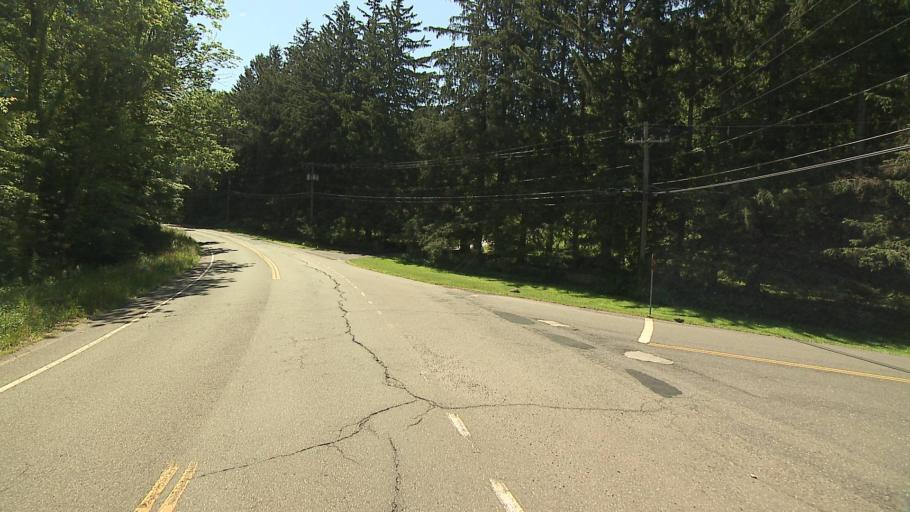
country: US
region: Connecticut
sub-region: Fairfield County
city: Ridgefield
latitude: 41.2904
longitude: -73.5246
